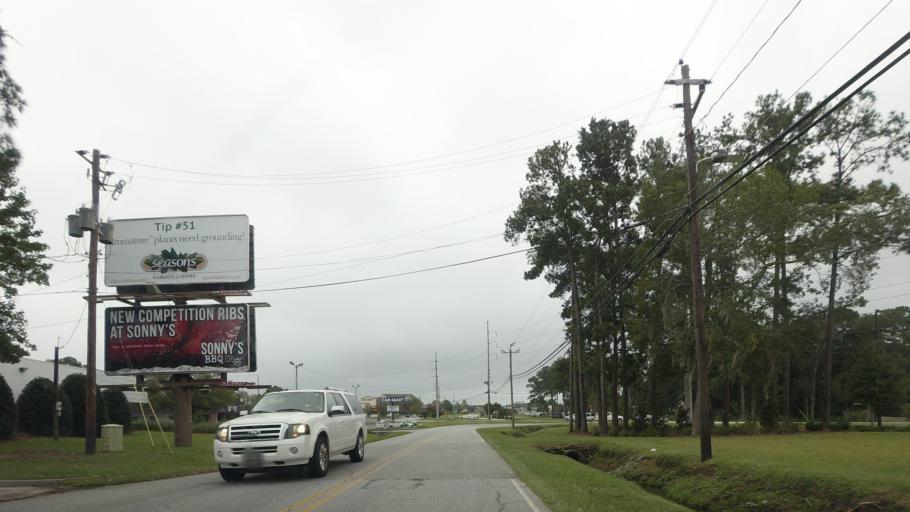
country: US
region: Georgia
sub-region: Lowndes County
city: Remerton
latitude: 30.8792
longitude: -83.2954
